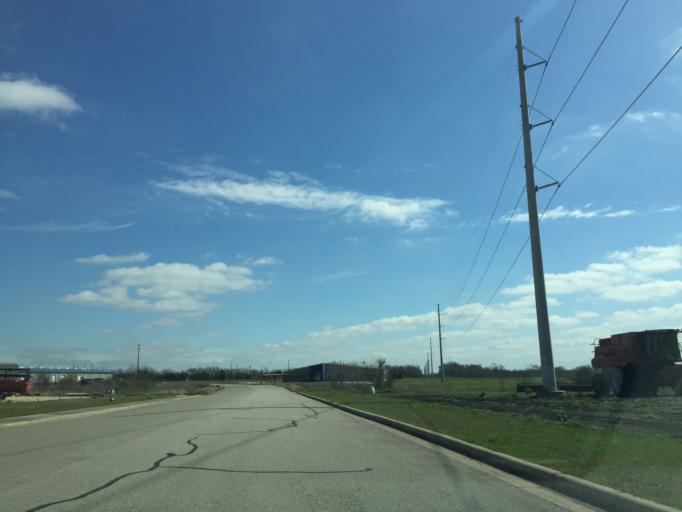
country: US
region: Texas
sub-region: Williamson County
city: Taylor
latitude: 30.5620
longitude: -97.4291
